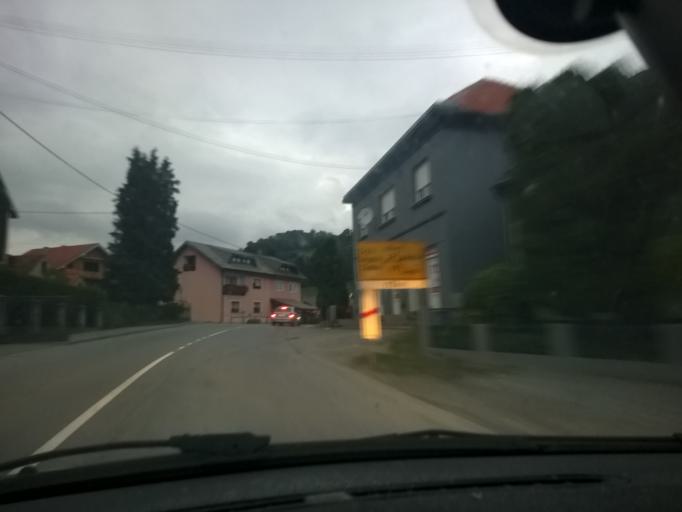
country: HR
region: Krapinsko-Zagorska
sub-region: Grad Krapina
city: Krapina
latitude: 46.1947
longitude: 15.8406
